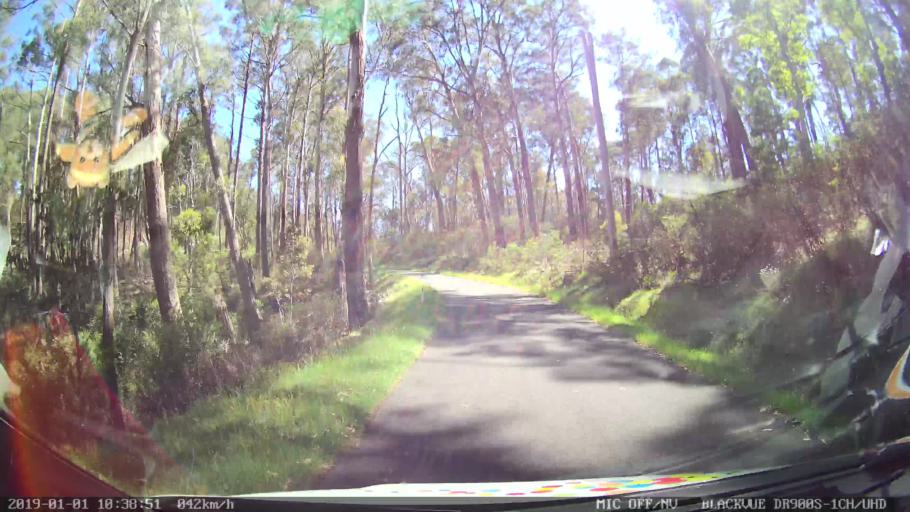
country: AU
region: New South Wales
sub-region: Snowy River
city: Jindabyne
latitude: -36.0429
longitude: 148.3013
